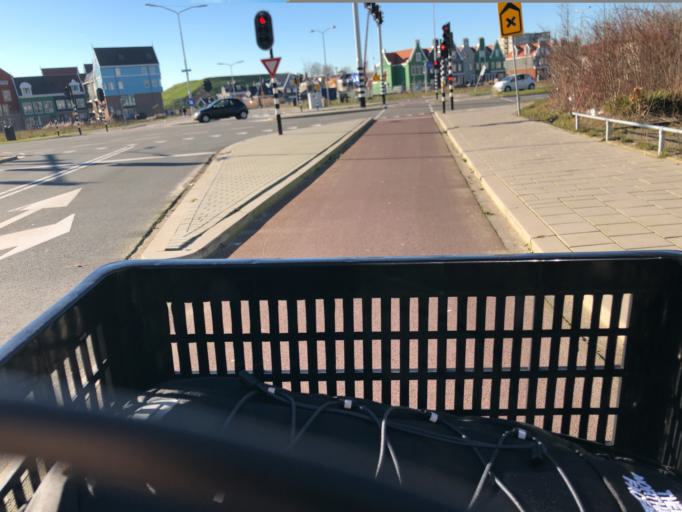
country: NL
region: North Holland
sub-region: Gemeente Zaanstad
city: Zaanstad
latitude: 52.4387
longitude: 4.8109
